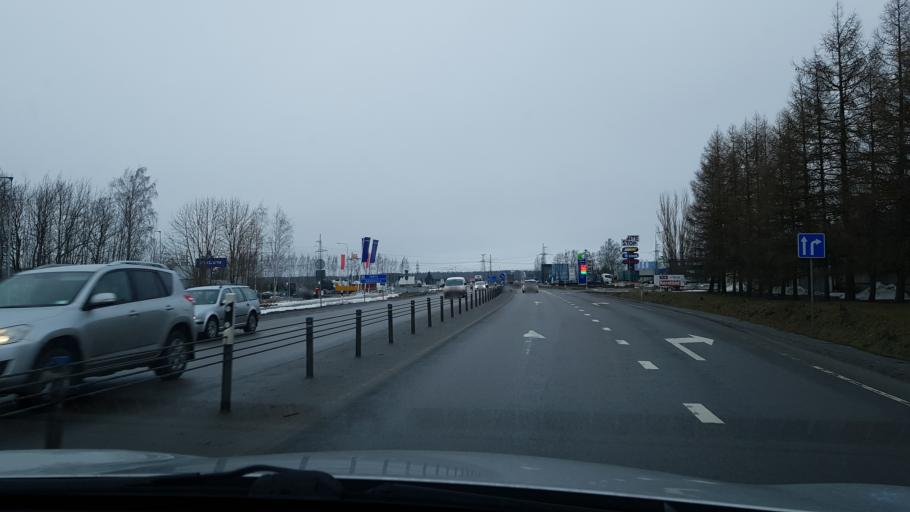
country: EE
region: Tartu
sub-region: Tartu linn
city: Tartu
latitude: 58.3736
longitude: 26.6781
